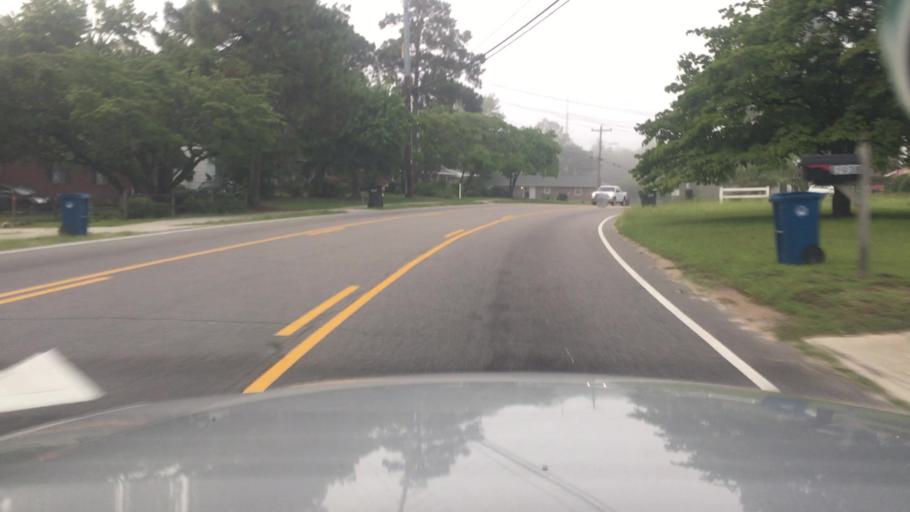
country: US
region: North Carolina
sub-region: Cumberland County
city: Hope Mills
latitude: 35.0220
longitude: -78.9404
